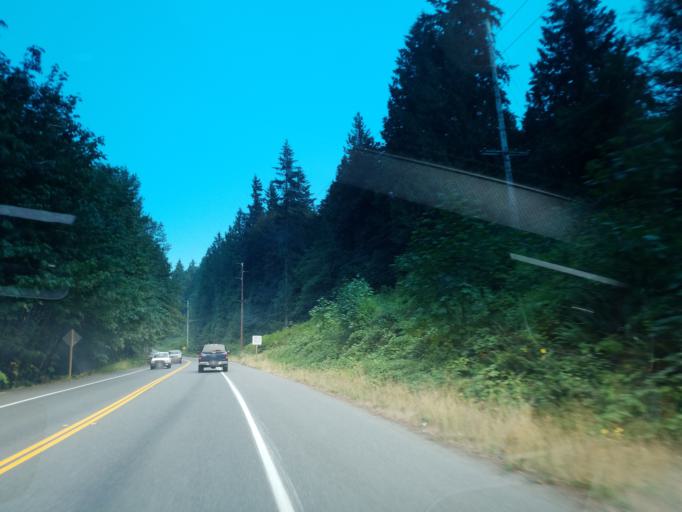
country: US
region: Washington
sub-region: King County
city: Sammamish
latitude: 47.6531
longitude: -122.0619
